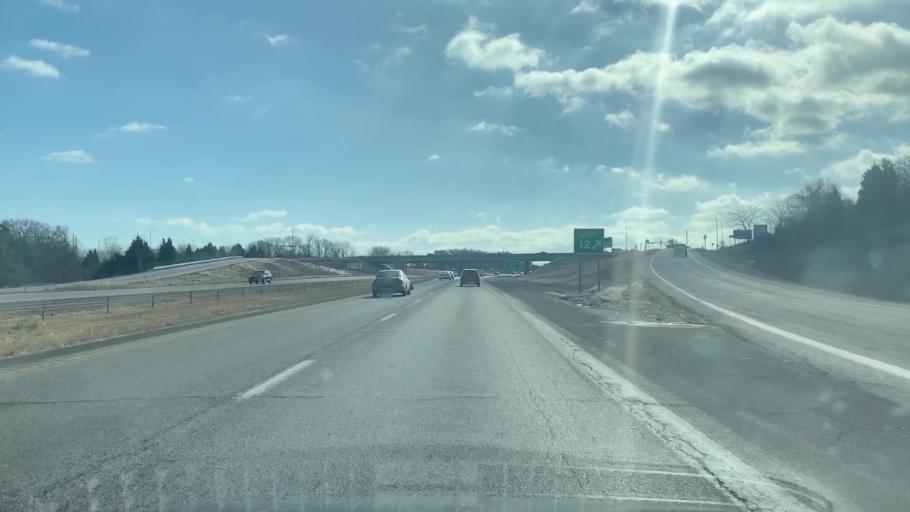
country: US
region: Missouri
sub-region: Jackson County
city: Lees Summit
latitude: 38.9852
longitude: -94.3569
